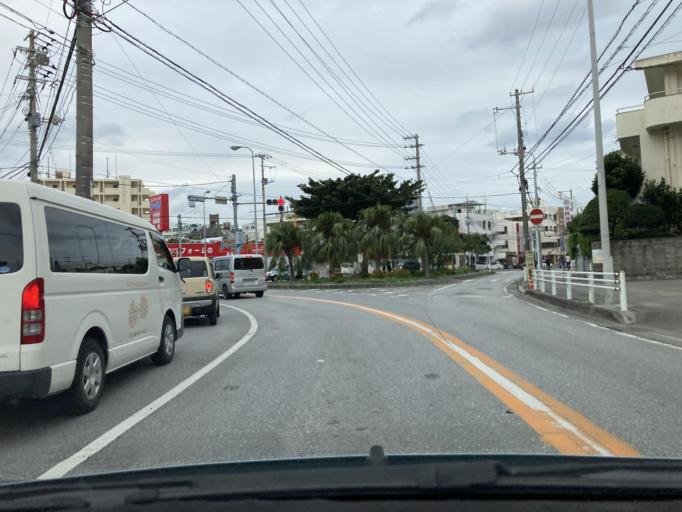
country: JP
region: Okinawa
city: Tomigusuku
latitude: 26.1937
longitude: 127.6765
